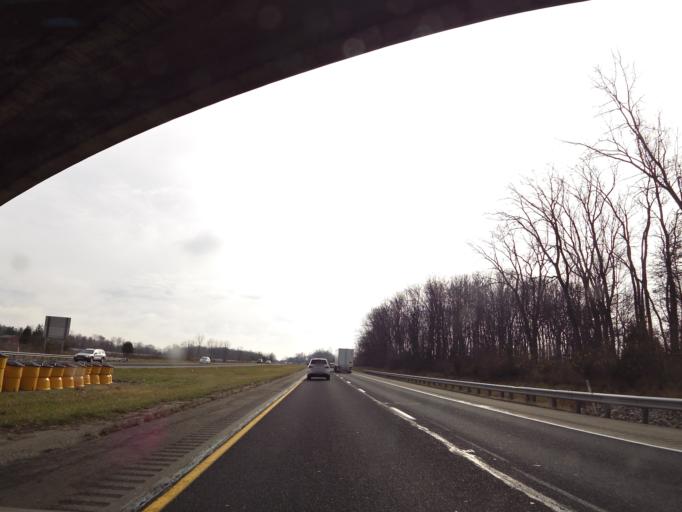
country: US
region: Indiana
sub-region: Marion County
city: Cumberland
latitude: 39.6967
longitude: -85.9908
